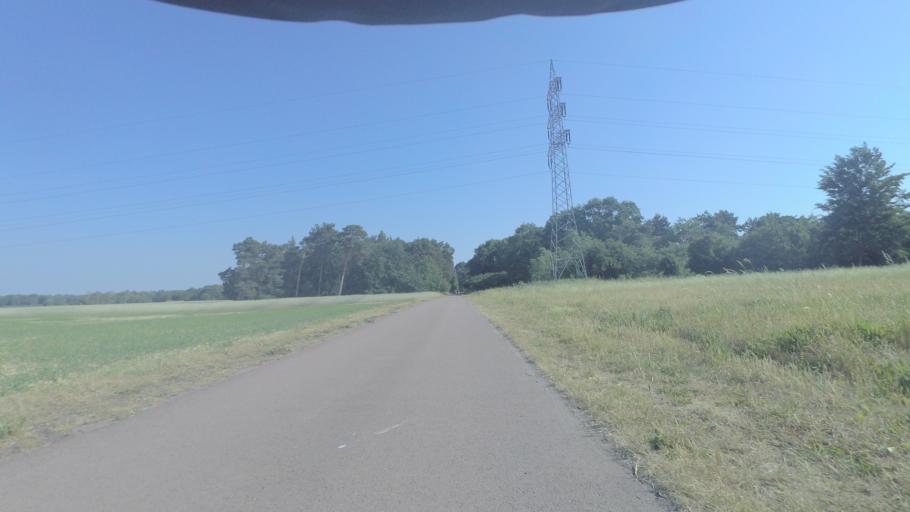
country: DE
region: Saxony-Anhalt
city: Quellendorf
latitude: 51.8203
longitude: 12.1586
